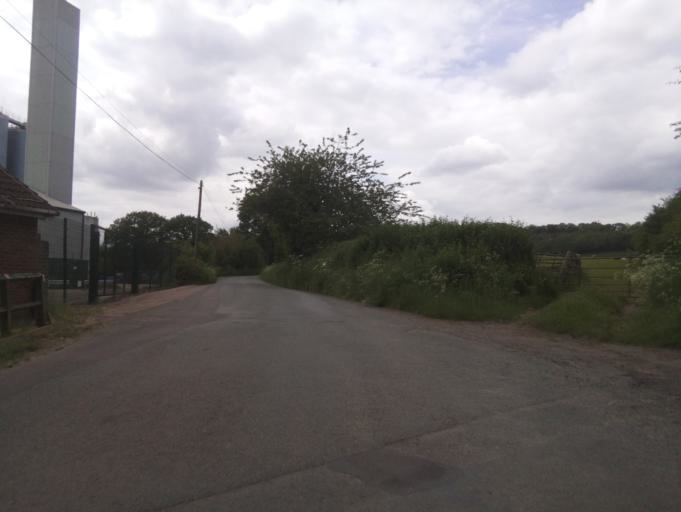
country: GB
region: England
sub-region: Herefordshire
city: Ledbury
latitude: 52.0338
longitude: -2.4454
